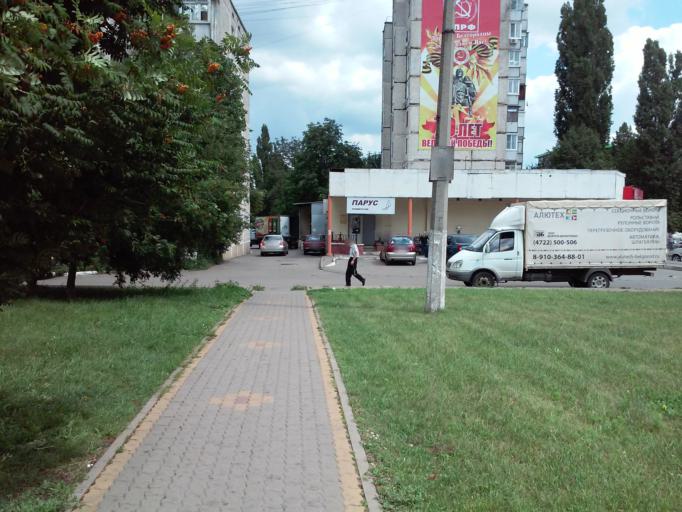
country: RU
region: Belgorod
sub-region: Belgorodskiy Rayon
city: Belgorod
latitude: 50.5732
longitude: 36.5852
